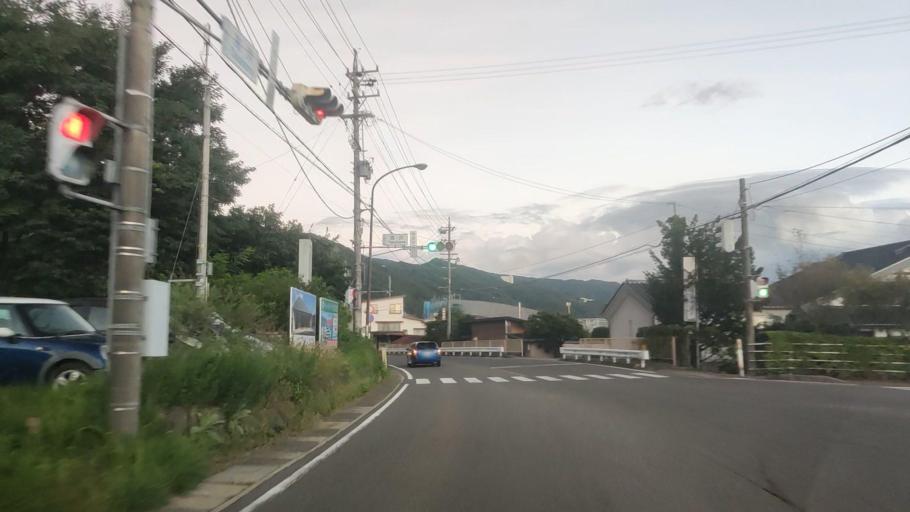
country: JP
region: Nagano
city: Suwa
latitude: 36.0675
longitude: 138.1001
